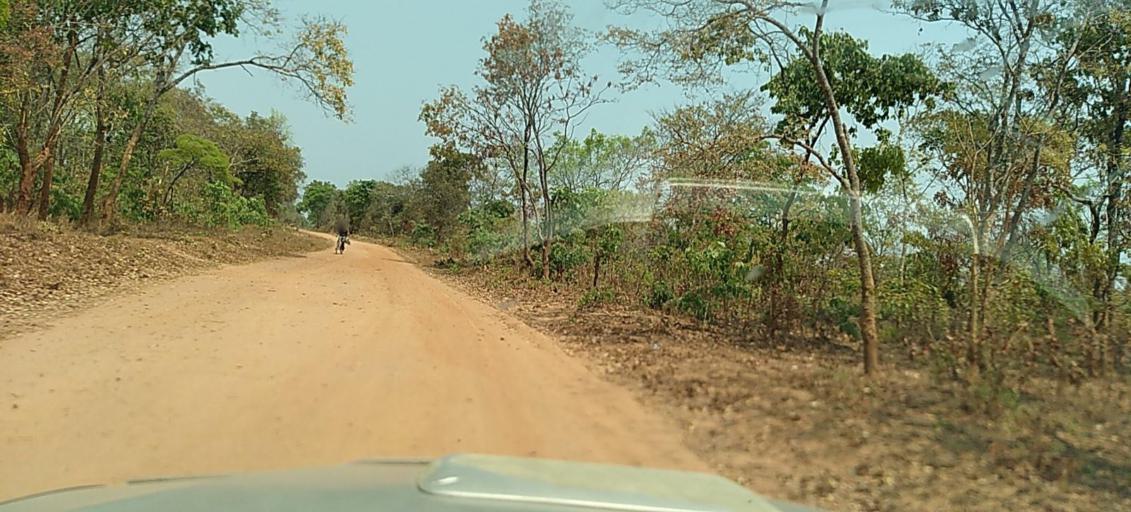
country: ZM
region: North-Western
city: Kasempa
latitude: -13.6904
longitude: 26.3227
